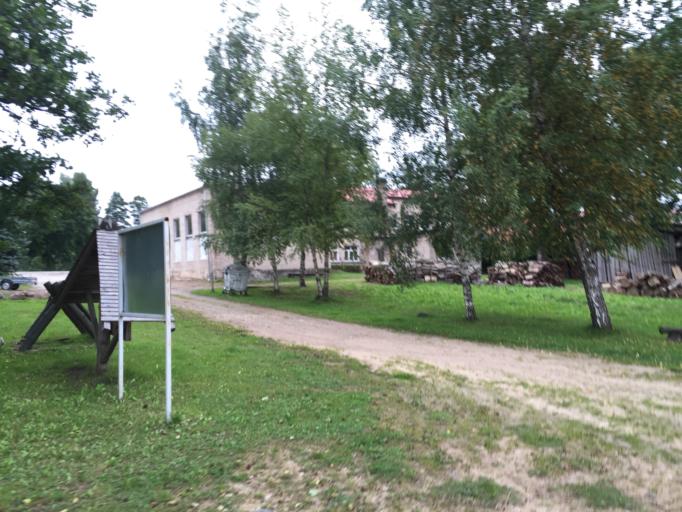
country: LV
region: Cibla
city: Cibla
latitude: 56.4085
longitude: 27.9254
